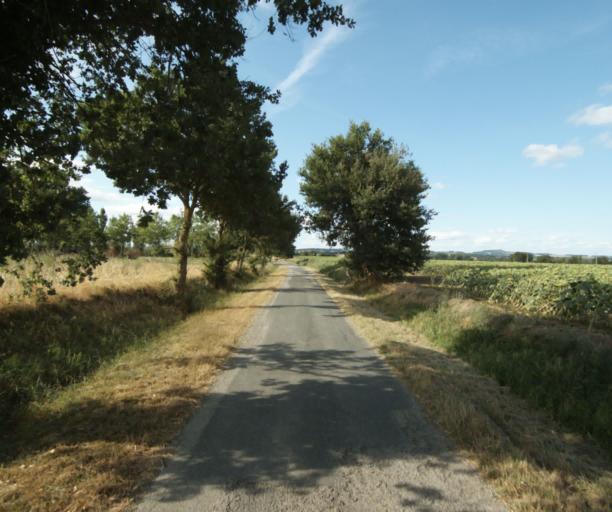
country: FR
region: Midi-Pyrenees
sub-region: Departement de la Haute-Garonne
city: Revel
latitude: 43.5073
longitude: 1.9971
